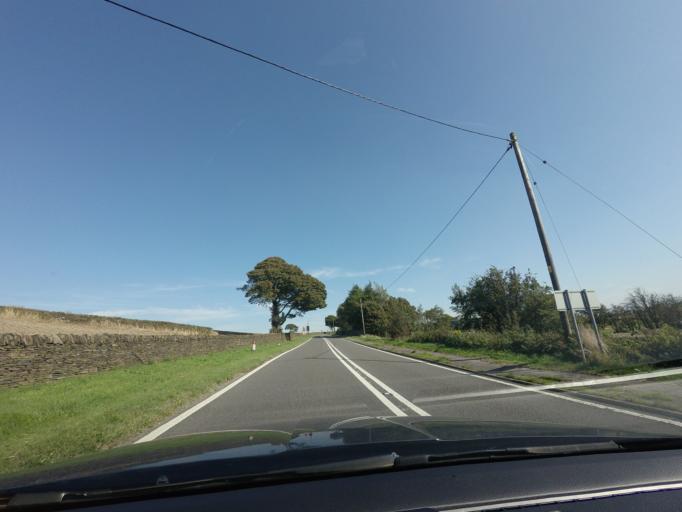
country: GB
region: England
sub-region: Derbyshire
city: Dronfield
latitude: 53.2383
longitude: -1.5392
